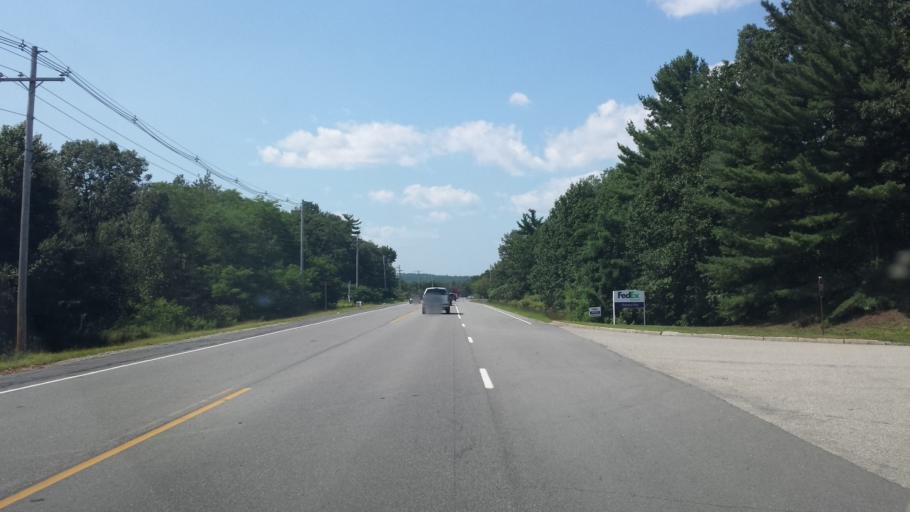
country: US
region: Maine
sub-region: York County
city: Biddeford
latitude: 43.4704
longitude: -70.4867
